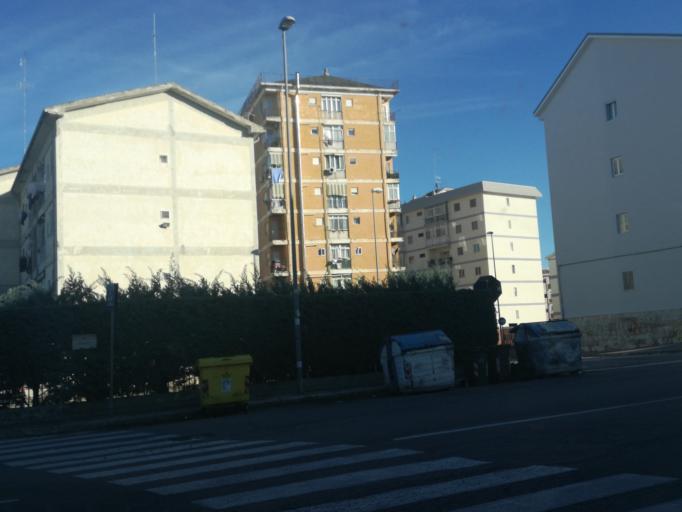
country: IT
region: Apulia
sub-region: Provincia di Bari
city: San Paolo
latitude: 41.1220
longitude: 16.7895
